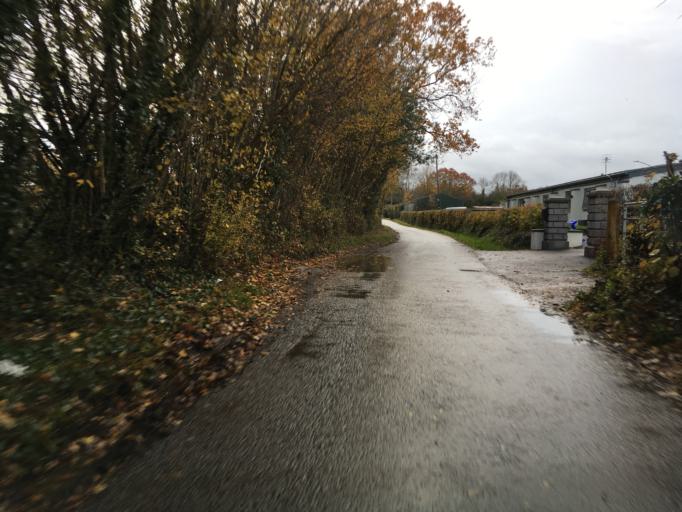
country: GB
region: England
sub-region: South Gloucestershire
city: Yate
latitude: 51.5529
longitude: -2.4280
